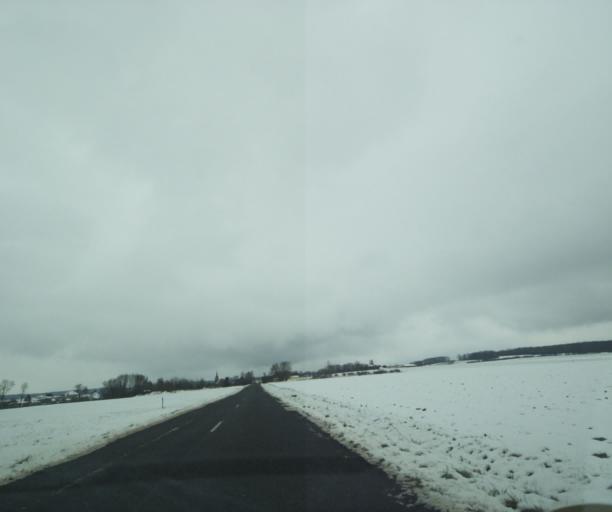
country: FR
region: Champagne-Ardenne
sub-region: Departement de la Haute-Marne
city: Laneuville-a-Remy
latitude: 48.4145
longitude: 4.8305
